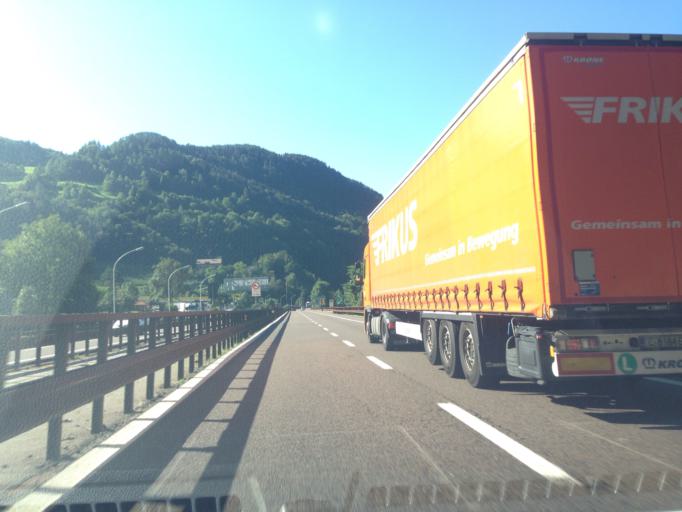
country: IT
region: Trentino-Alto Adige
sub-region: Bolzano
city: Ponte Gardena
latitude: 46.5725
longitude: 11.5231
